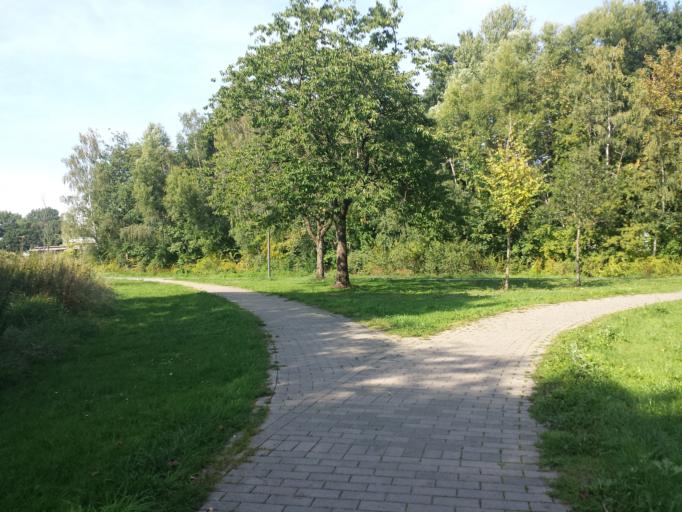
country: DE
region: Bremen
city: Bremen
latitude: 53.0335
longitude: 8.8193
